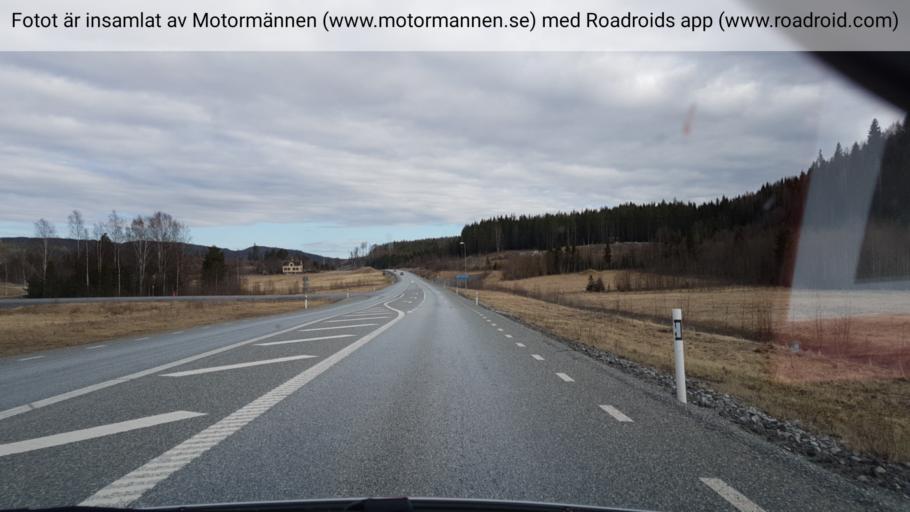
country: SE
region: Vaesternorrland
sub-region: Kramfors Kommun
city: Bollstabruk
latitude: 63.0400
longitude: 17.6465
